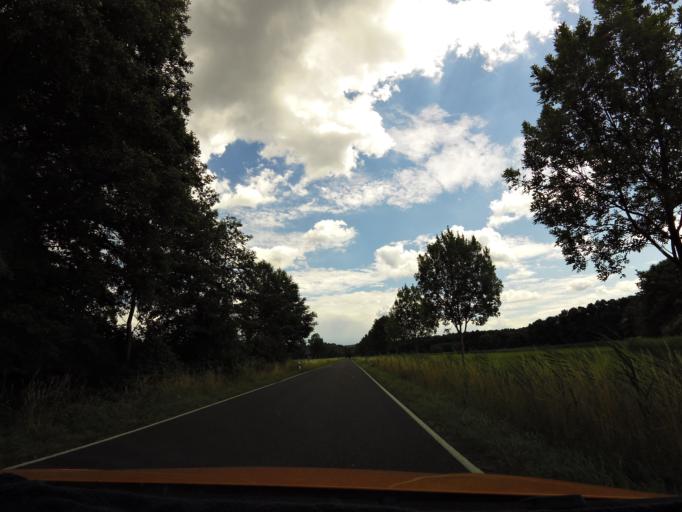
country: DE
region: Brandenburg
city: Munchehofe
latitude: 52.2492
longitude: 13.7933
